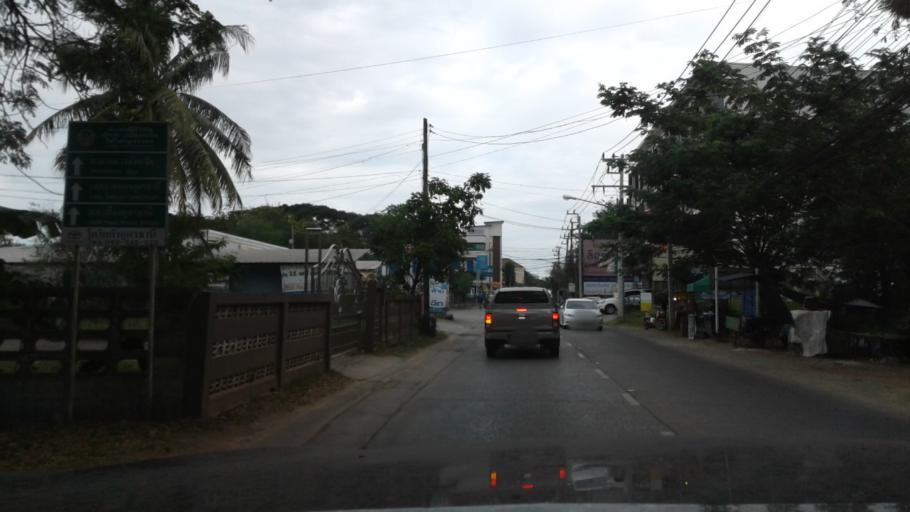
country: TH
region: Changwat Udon Thani
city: Udon Thani
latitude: 17.3989
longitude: 102.7717
